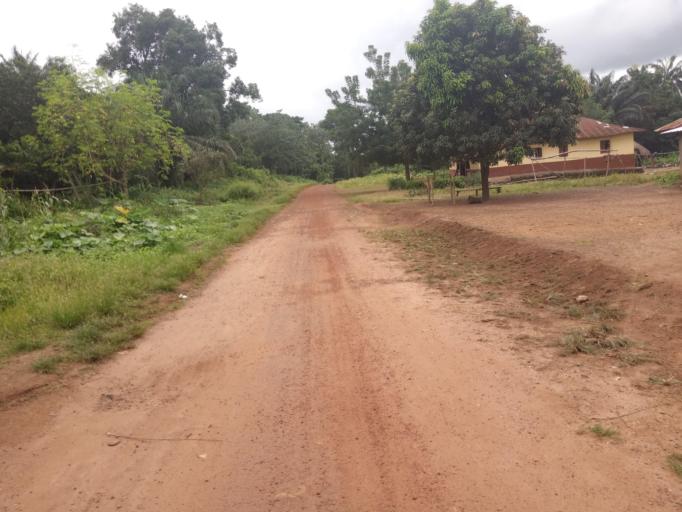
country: SL
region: Northern Province
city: Kamakwie
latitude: 9.5053
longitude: -12.2607
